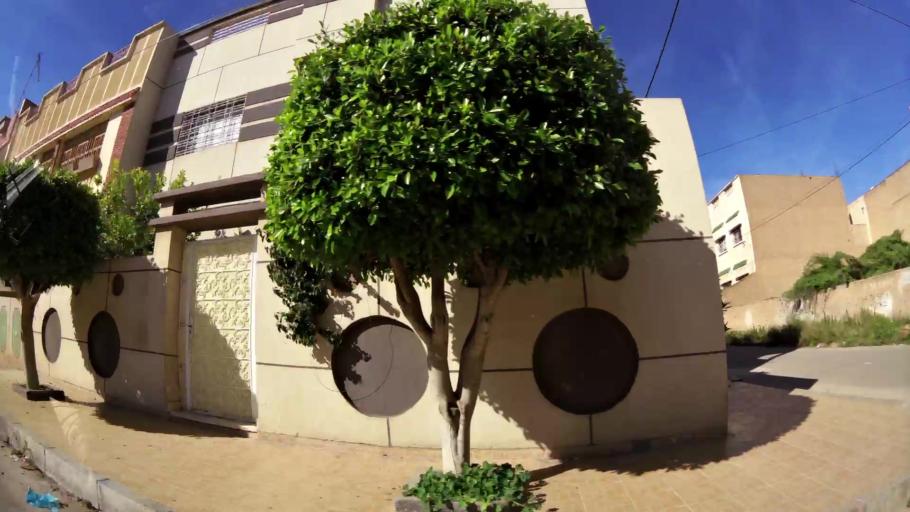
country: MA
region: Oriental
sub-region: Oujda-Angad
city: Oujda
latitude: 34.6680
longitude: -1.9154
